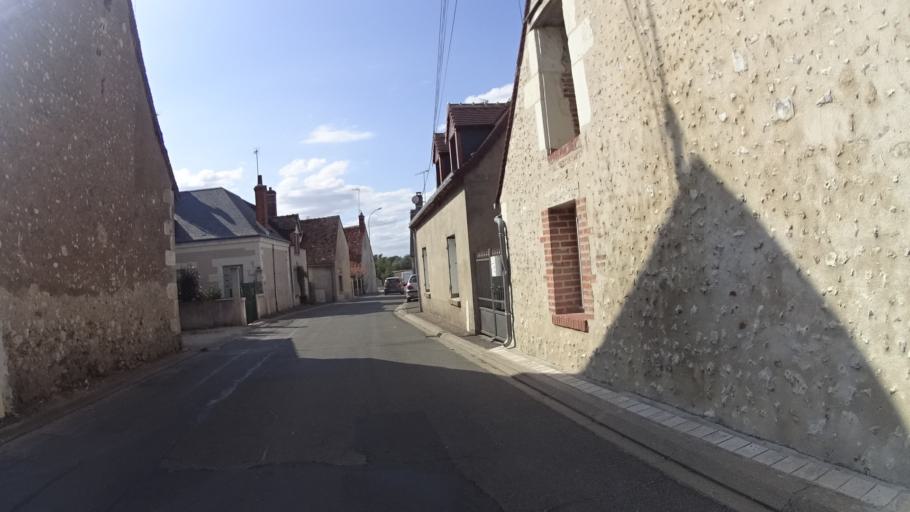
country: FR
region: Centre
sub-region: Departement du Loir-et-Cher
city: Chaumont-sur-Loire
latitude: 47.4825
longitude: 1.1926
